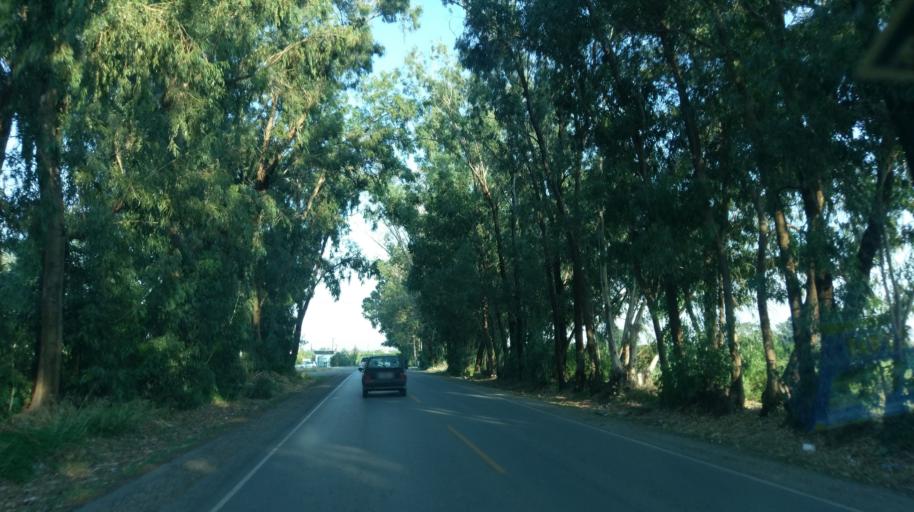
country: CY
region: Lefkosia
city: Lefka
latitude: 35.1570
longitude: 32.8934
